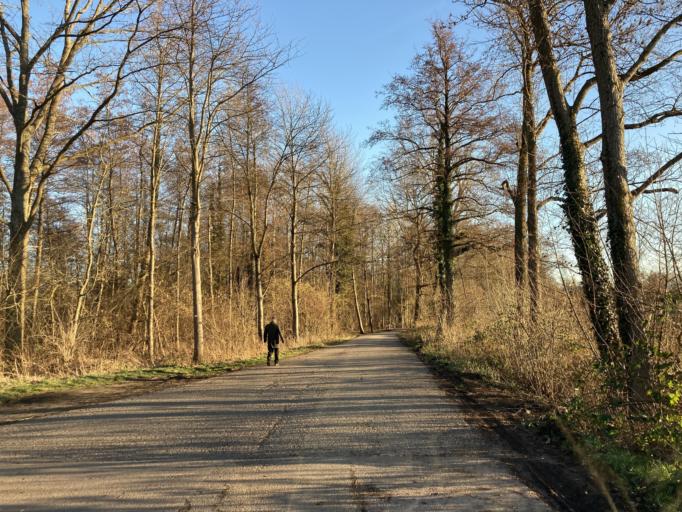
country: DE
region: Baden-Wuerttemberg
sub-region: Freiburg Region
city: Umkirch
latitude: 48.0555
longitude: 7.7699
